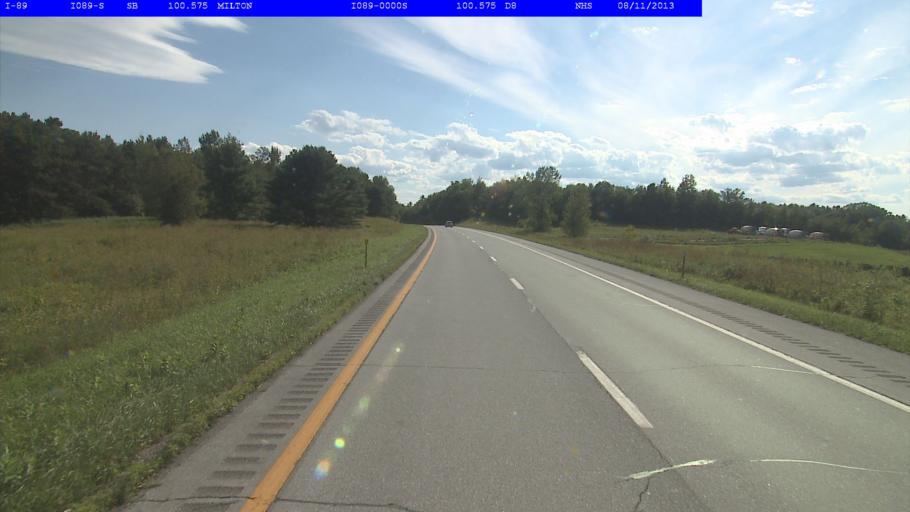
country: US
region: Vermont
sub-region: Chittenden County
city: Milton
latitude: 44.6256
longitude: -73.1550
